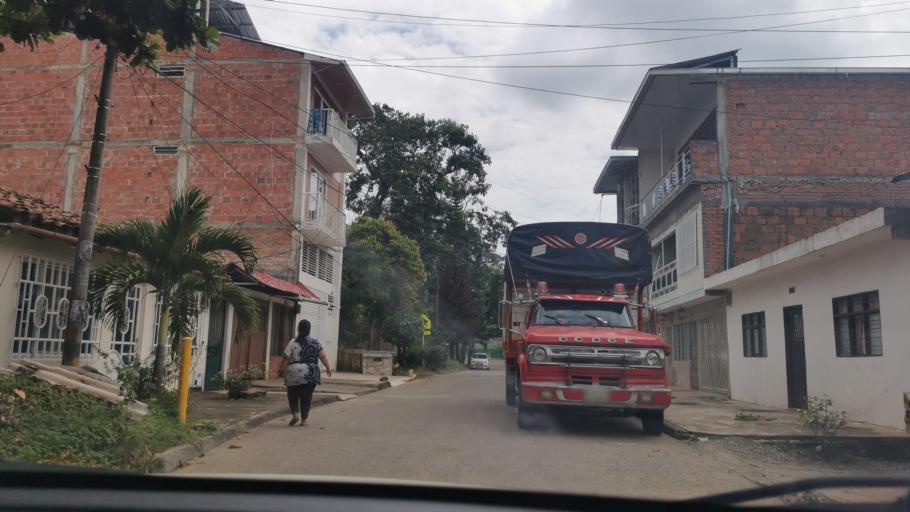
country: CO
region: Valle del Cauca
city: Jamundi
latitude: 3.2647
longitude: -76.5418
